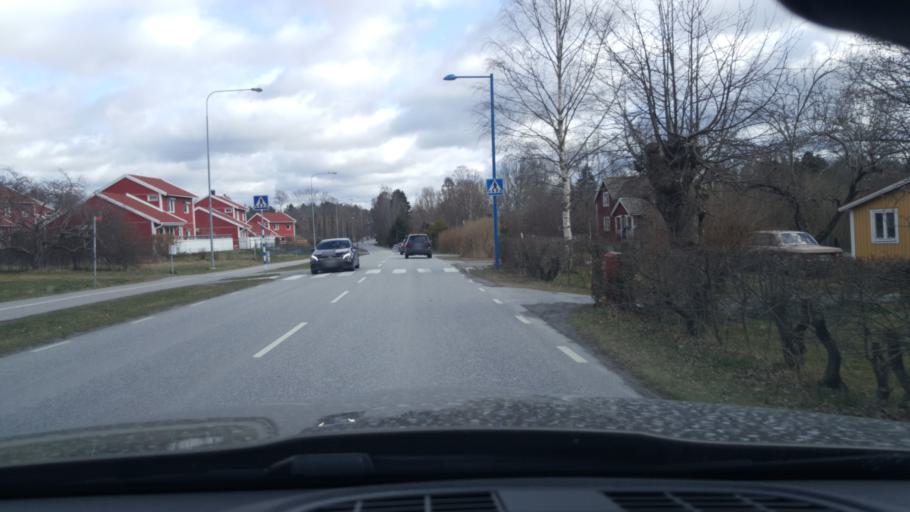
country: SE
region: Stockholm
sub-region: Osterakers Kommun
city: Akersberga
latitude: 59.4884
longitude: 18.2876
